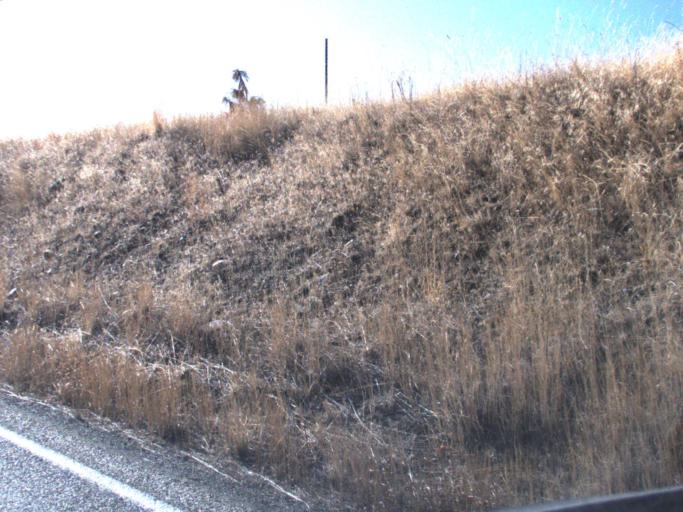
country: US
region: Washington
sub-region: Ferry County
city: Republic
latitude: 48.7368
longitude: -118.6602
